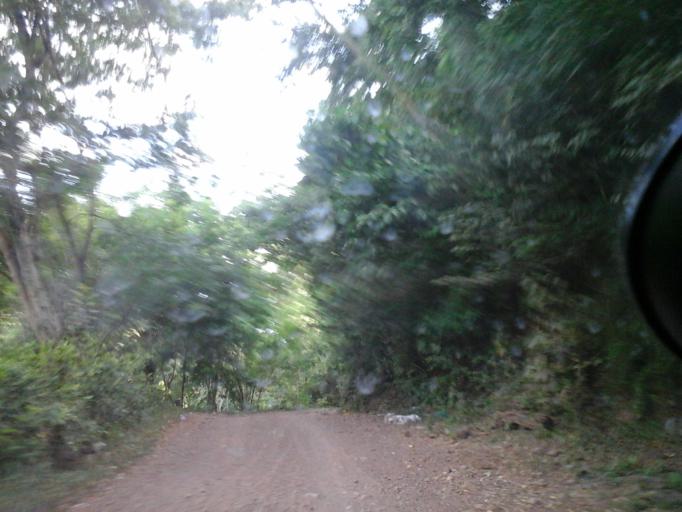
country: CO
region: Cesar
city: San Diego
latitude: 10.2428
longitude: -73.1372
